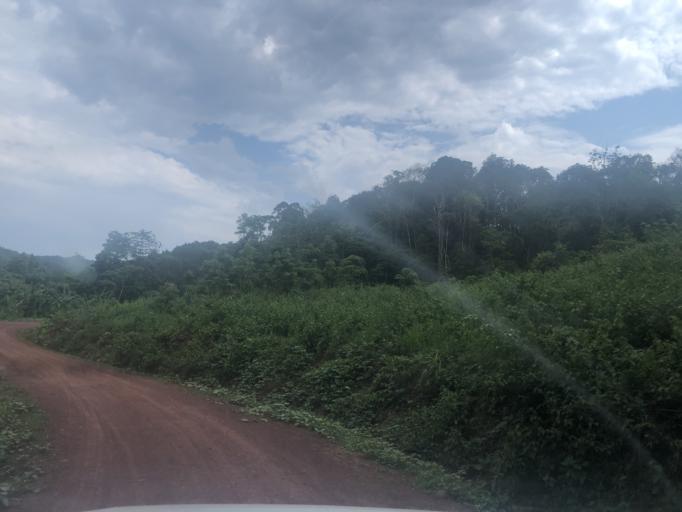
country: LA
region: Phongsali
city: Phongsali
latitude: 21.2751
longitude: 101.9966
